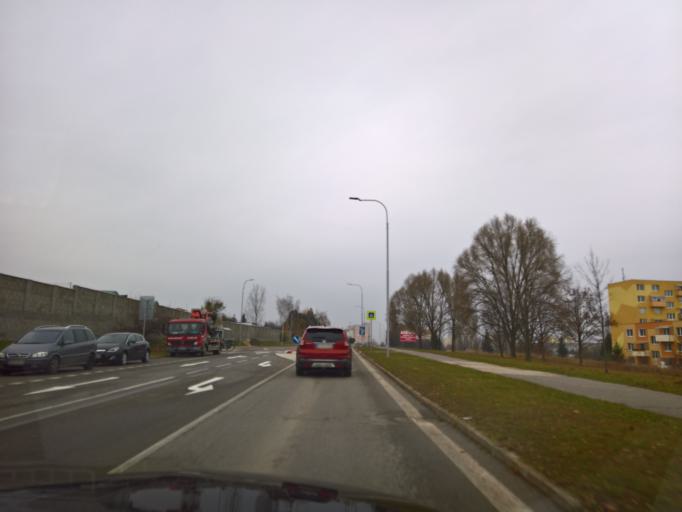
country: SK
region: Nitriansky
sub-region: Okres Nitra
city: Nitra
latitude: 48.2991
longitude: 18.0533
